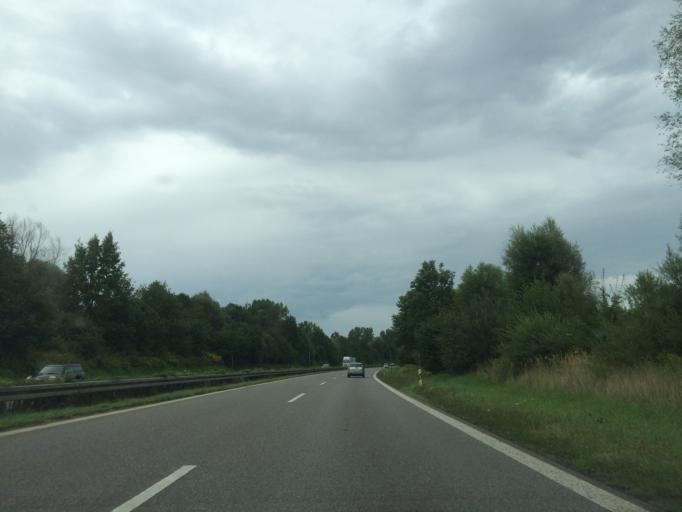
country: DE
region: Baden-Wuerttemberg
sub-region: Tuebingen Region
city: Berg
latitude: 47.8133
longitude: 9.6069
